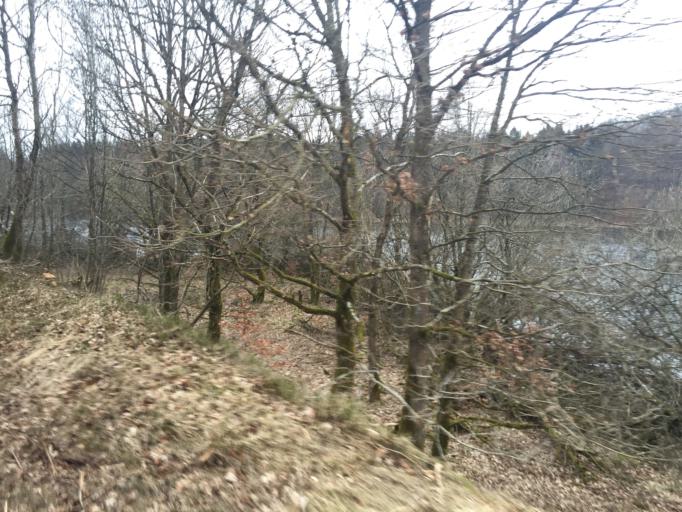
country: DK
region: Central Jutland
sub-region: Silkeborg Kommune
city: Virklund
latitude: 56.0287
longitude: 9.4857
